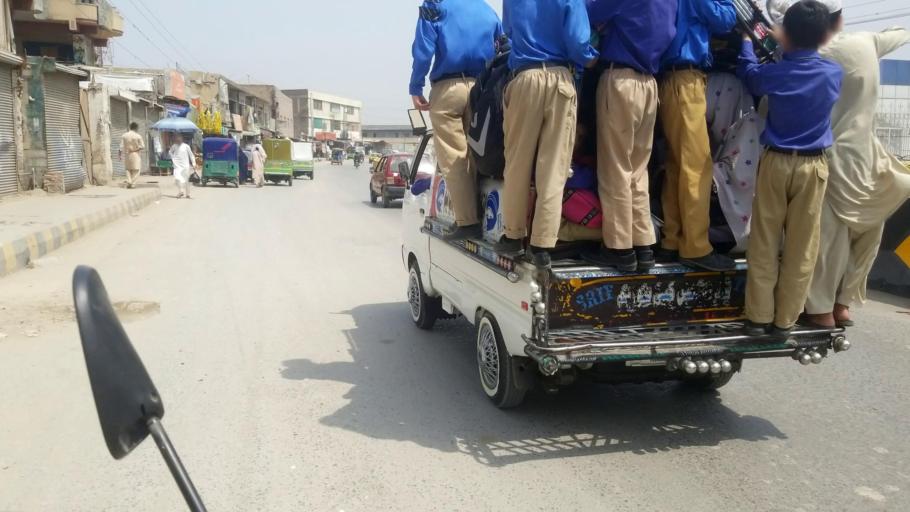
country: PK
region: Khyber Pakhtunkhwa
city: Peshawar
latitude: 34.0291
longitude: 71.5756
